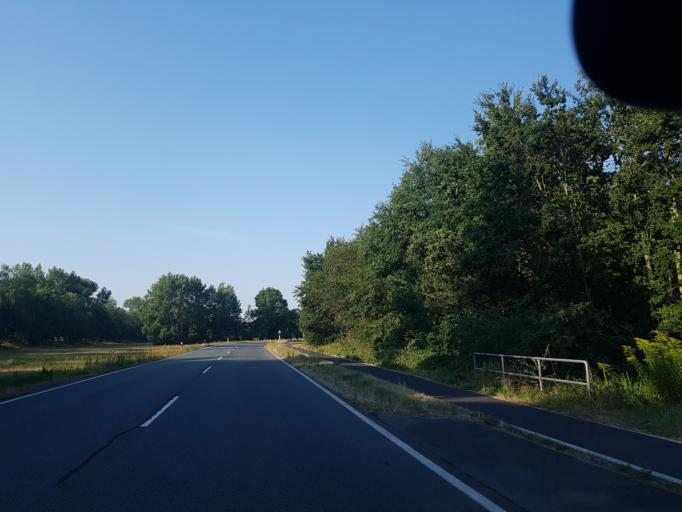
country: DE
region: Saxony
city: Nauwalde
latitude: 51.3941
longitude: 13.4210
